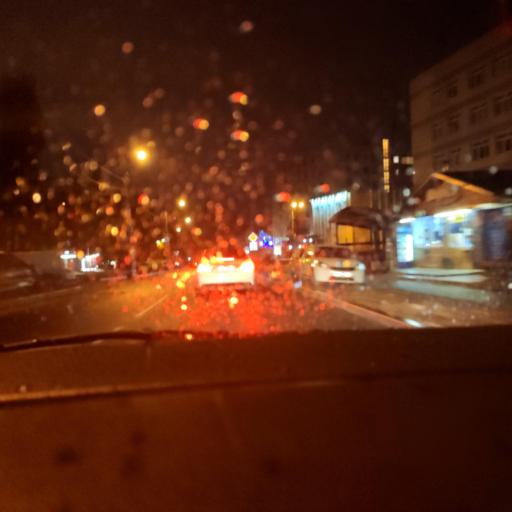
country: RU
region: Voronezj
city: Voronezh
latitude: 51.6738
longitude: 39.2504
